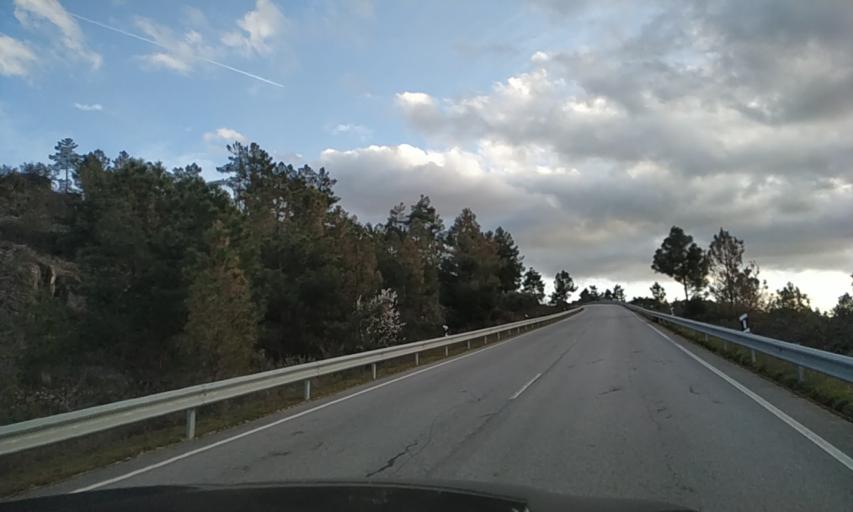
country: PT
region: Braganca
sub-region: Carrazeda de Ansiaes
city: Carrazeda de Anciaes
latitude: 41.2864
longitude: -7.3369
